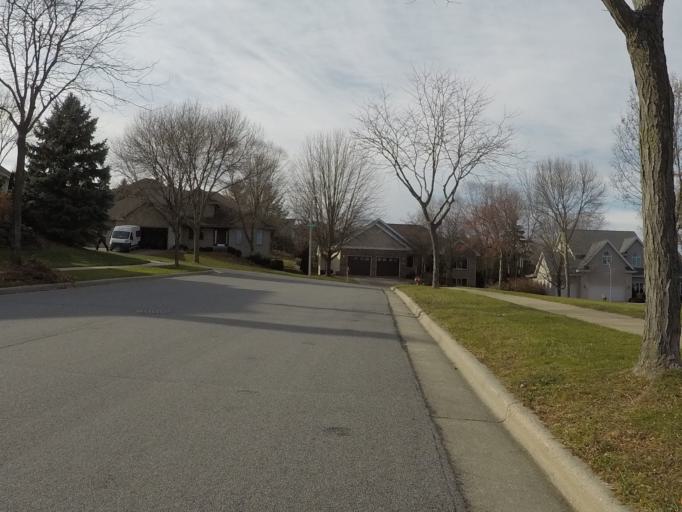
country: US
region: Wisconsin
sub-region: Dane County
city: Middleton
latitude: 43.0786
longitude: -89.5410
